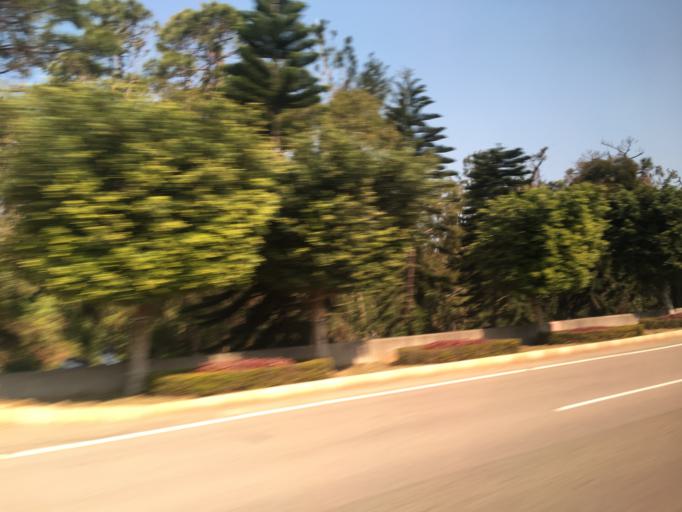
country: TW
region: Fukien
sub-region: Kinmen
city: Jincheng
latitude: 24.4361
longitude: 118.3563
